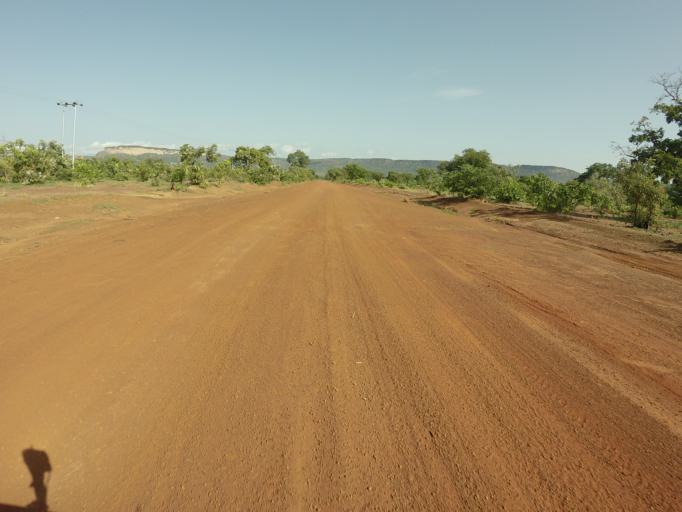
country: GH
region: Upper East
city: Bawku
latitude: 10.6822
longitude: -0.2143
